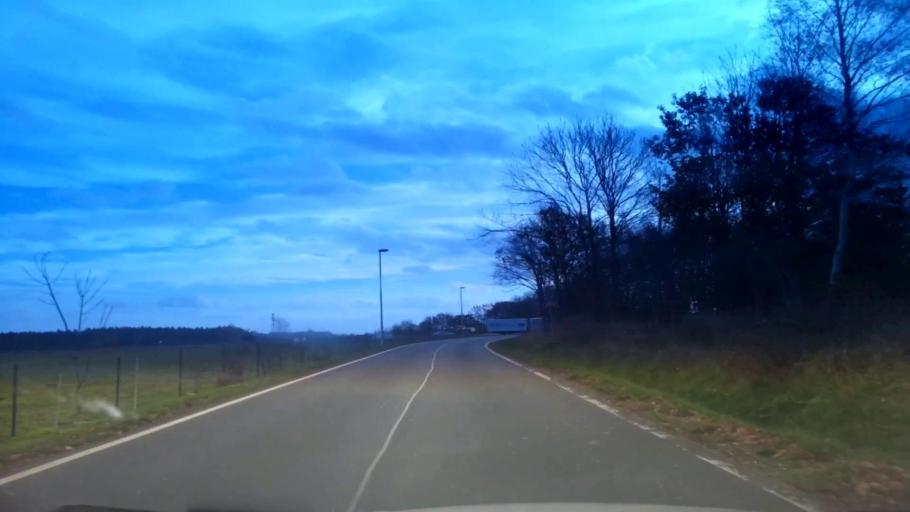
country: CZ
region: Karlovarsky
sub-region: Okres Cheb
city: Cheb
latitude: 50.0551
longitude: 12.3708
